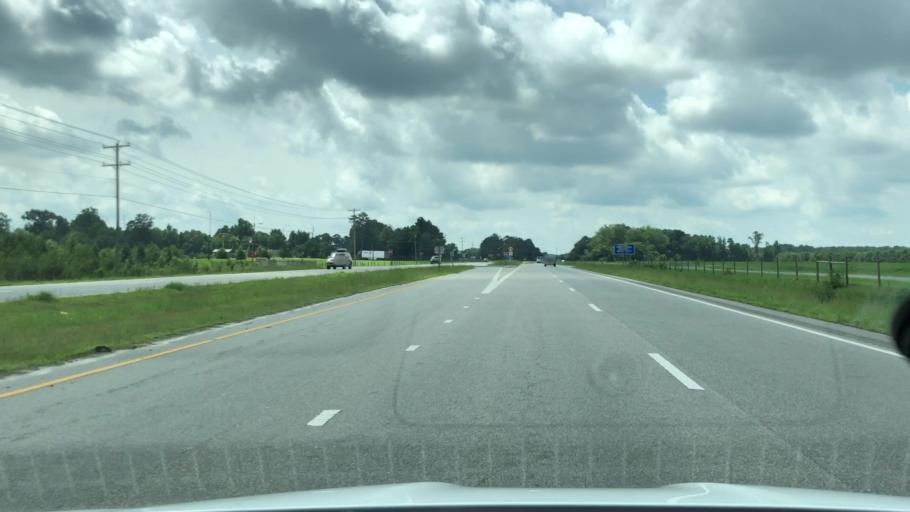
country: US
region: North Carolina
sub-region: Beaufort County
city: Washington
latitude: 35.4939
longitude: -77.1061
